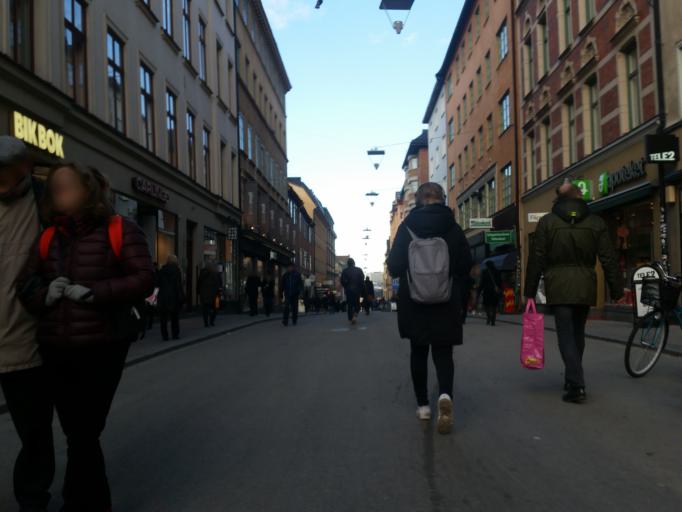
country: SE
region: Stockholm
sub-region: Stockholms Kommun
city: Stockholm
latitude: 59.3172
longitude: 18.0718
